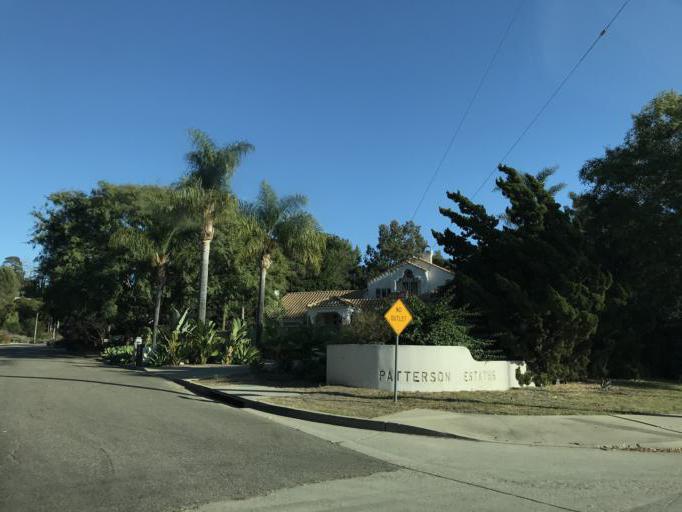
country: US
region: California
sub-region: Santa Barbara County
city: Goleta
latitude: 34.4545
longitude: -119.8078
